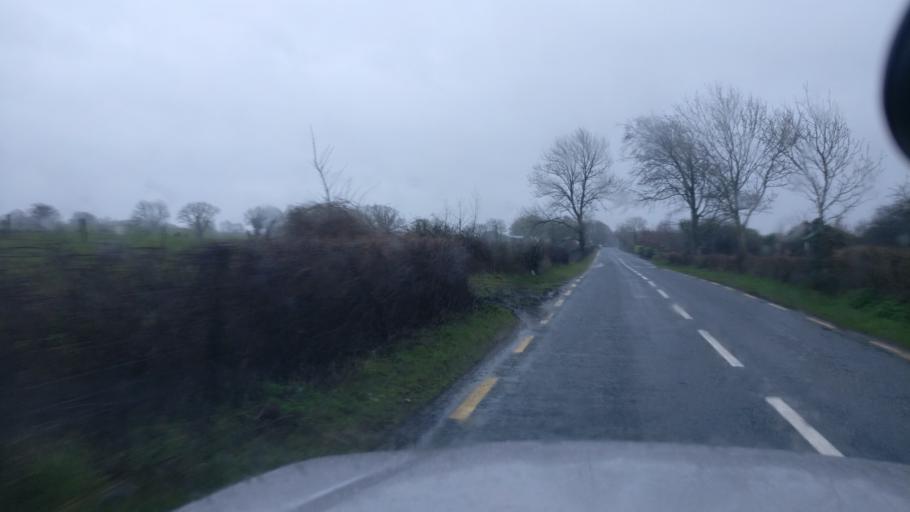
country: IE
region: Connaught
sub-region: County Galway
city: Ballinasloe
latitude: 53.2661
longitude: -8.1933
